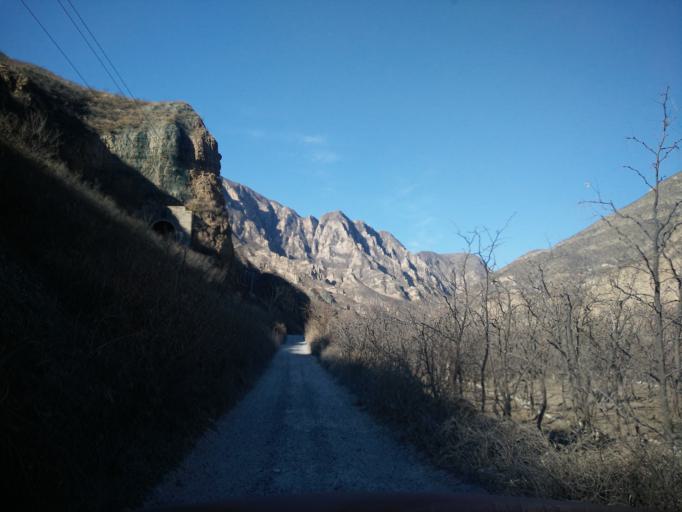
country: CN
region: Beijing
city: Yanjiatai
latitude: 40.1650
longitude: 115.6522
